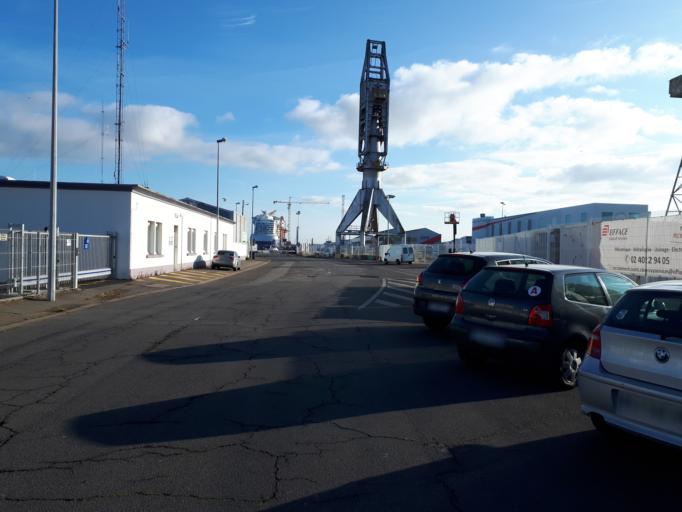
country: FR
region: Pays de la Loire
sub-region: Departement de la Loire-Atlantique
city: Saint-Nazaire
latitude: 47.2775
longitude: -2.1988
